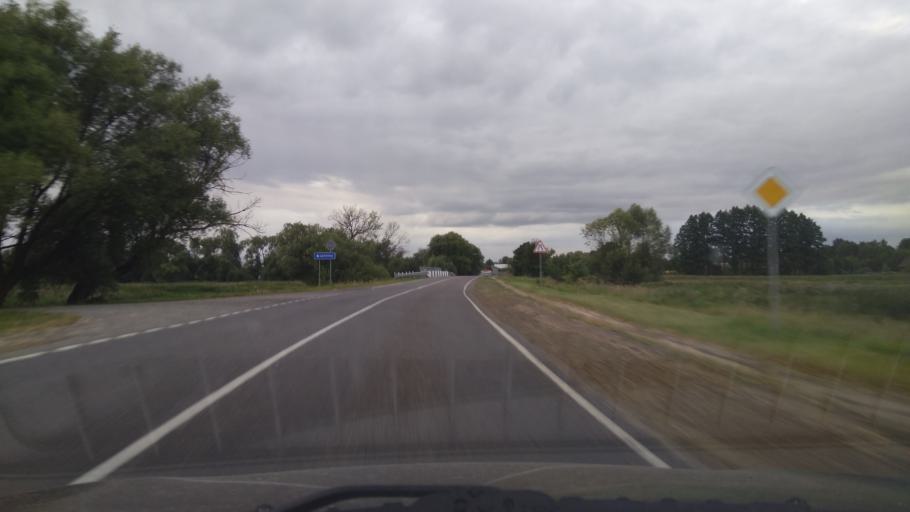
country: BY
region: Brest
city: Byaroza
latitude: 52.4181
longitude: 24.9800
